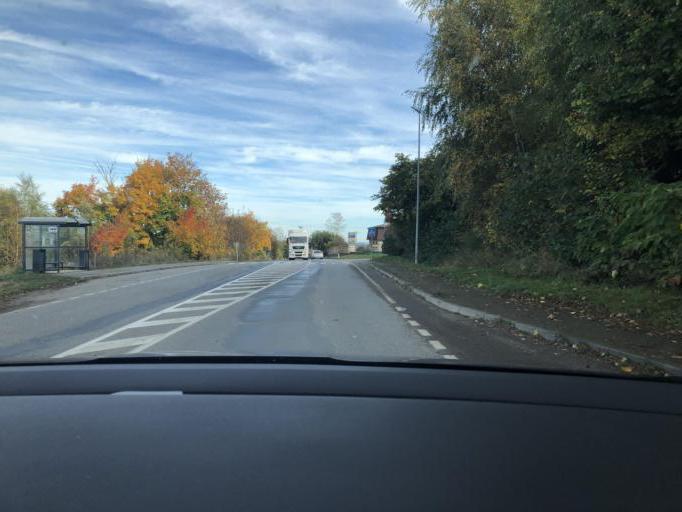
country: CZ
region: Central Bohemia
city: Divisov
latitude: 49.8005
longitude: 14.8976
